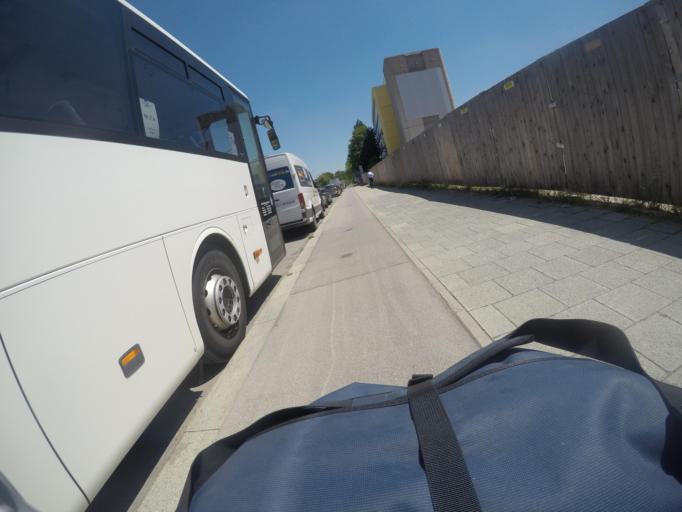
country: DE
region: Bavaria
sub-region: Upper Bavaria
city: Pullach im Isartal
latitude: 48.0984
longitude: 11.5165
